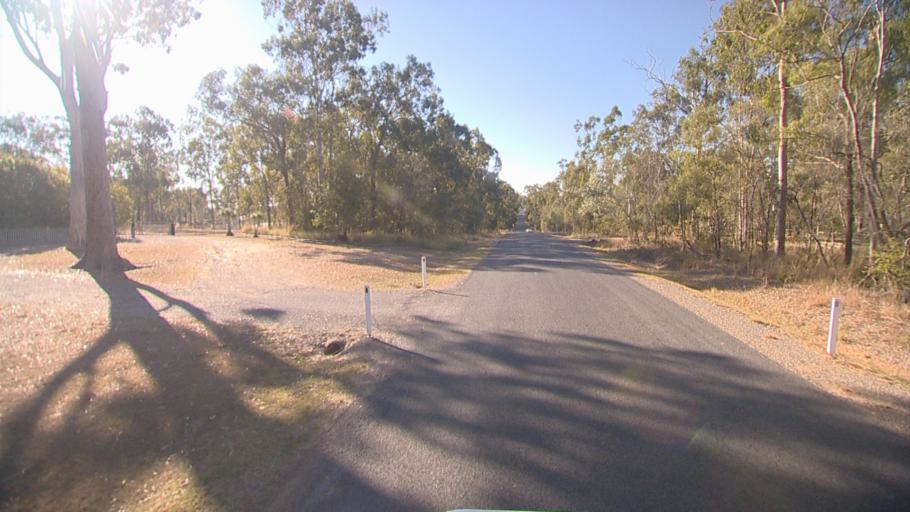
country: AU
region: Queensland
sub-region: Logan
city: North Maclean
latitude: -27.7981
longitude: 153.0259
